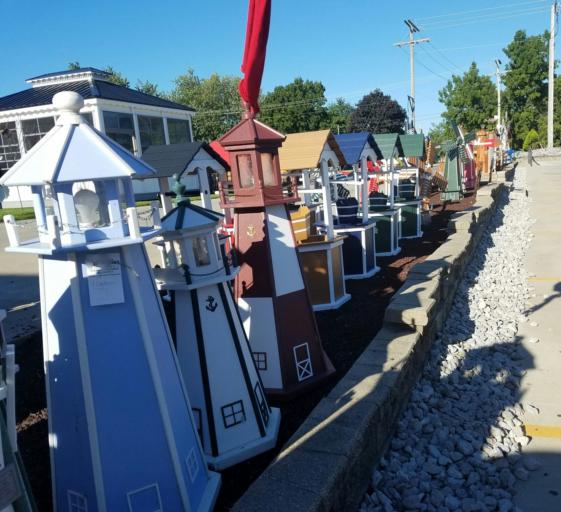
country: US
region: Indiana
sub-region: LaGrange County
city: Topeka
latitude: 41.6582
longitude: -85.5795
